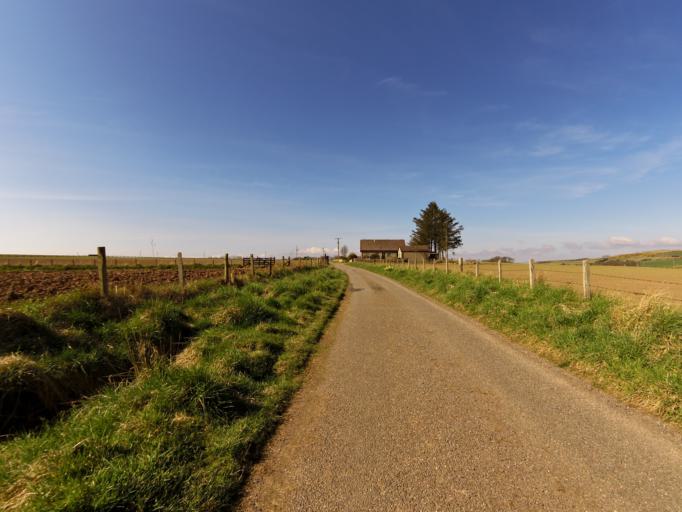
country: GB
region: Scotland
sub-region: Angus
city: Montrose
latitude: 56.7701
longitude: -2.4220
